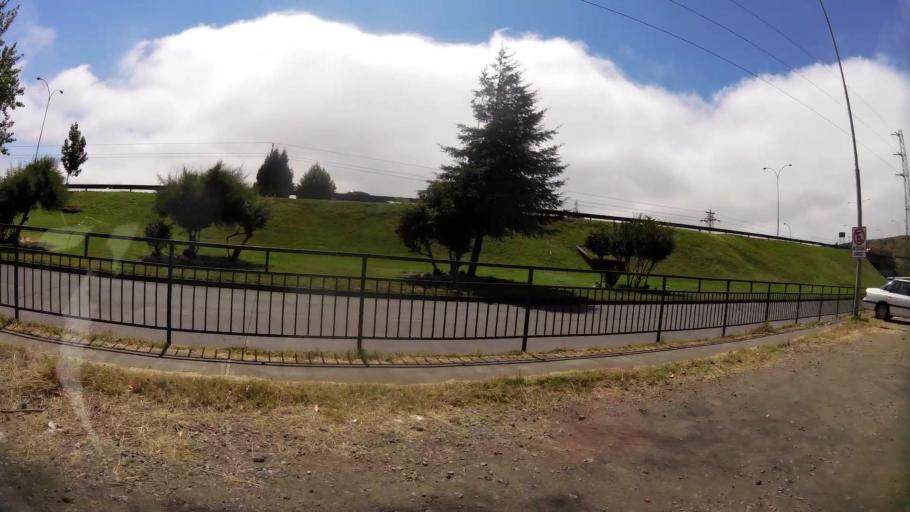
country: CL
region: Biobio
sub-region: Provincia de Concepcion
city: Concepcion
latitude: -36.7994
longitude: -73.0497
